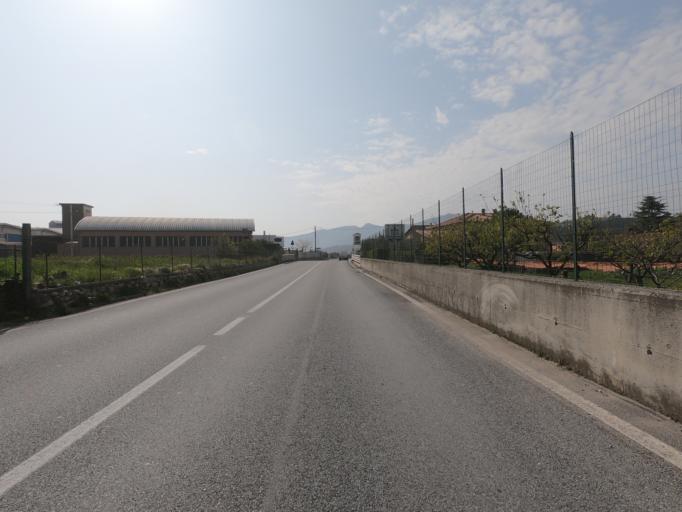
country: IT
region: Liguria
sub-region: Provincia di Savona
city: Cisano
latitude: 44.0783
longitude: 8.1572
